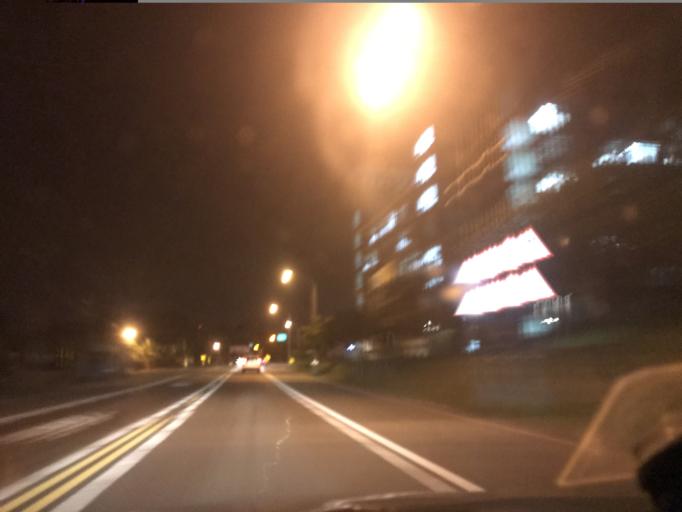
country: TW
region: Taiwan
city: Daxi
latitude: 24.9026
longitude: 121.2307
